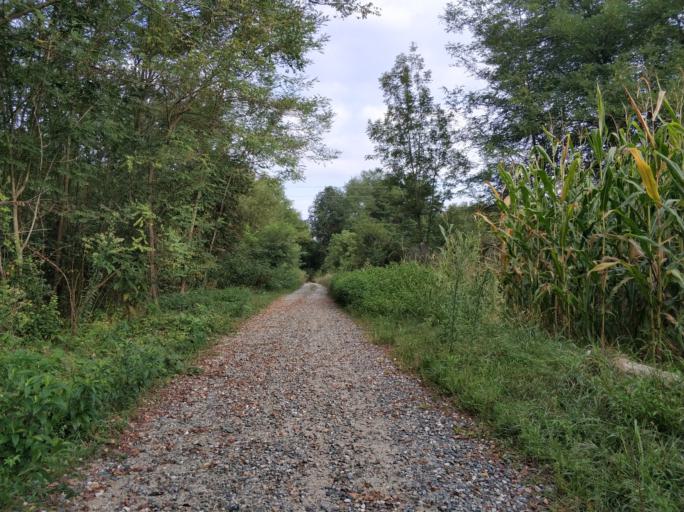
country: IT
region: Piedmont
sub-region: Provincia di Torino
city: Robassomero
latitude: 45.2157
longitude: 7.5690
